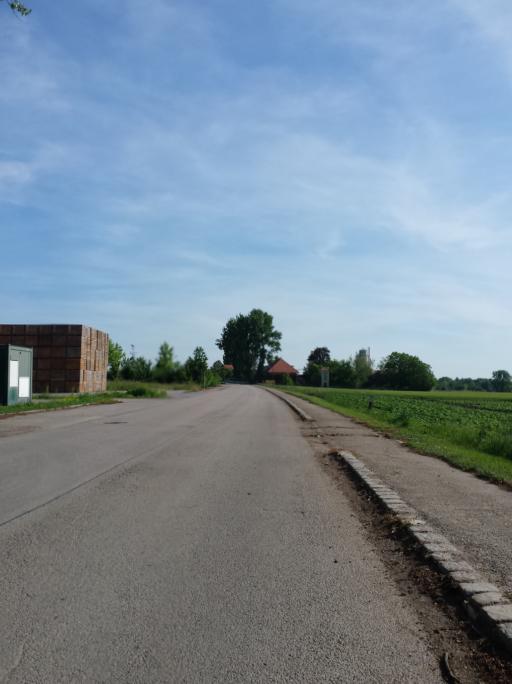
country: AT
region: Lower Austria
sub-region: Politischer Bezirk Hollabrunn
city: Wullersdorf
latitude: 48.6181
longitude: 16.0943
